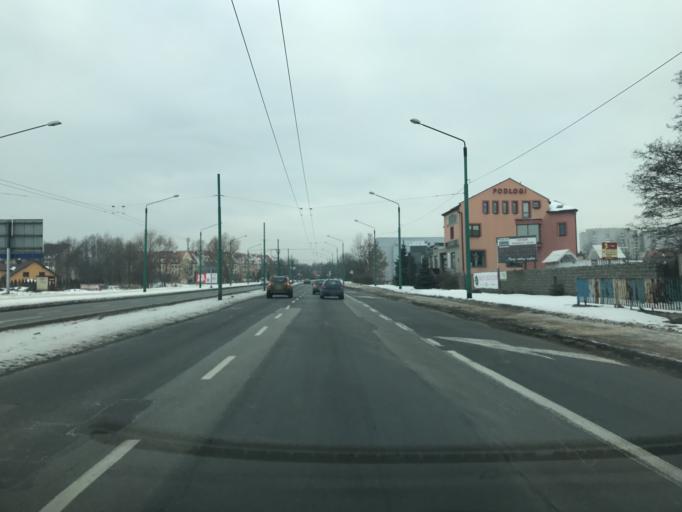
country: PL
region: Silesian Voivodeship
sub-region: Tychy
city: Cielmice
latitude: 50.1009
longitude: 19.0037
